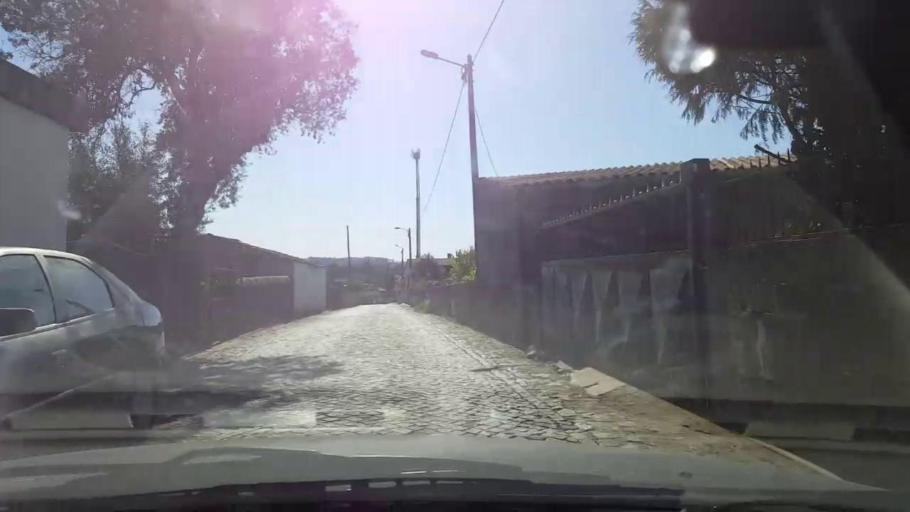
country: PT
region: Braga
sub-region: Vila Nova de Famalicao
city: Ribeirao
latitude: 41.3573
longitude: -8.6270
